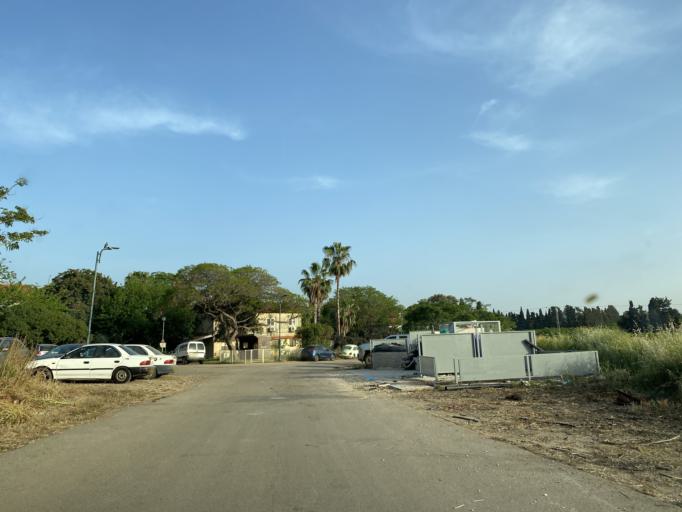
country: IL
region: Tel Aviv
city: Herzliyya
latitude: 32.1566
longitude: 34.8287
